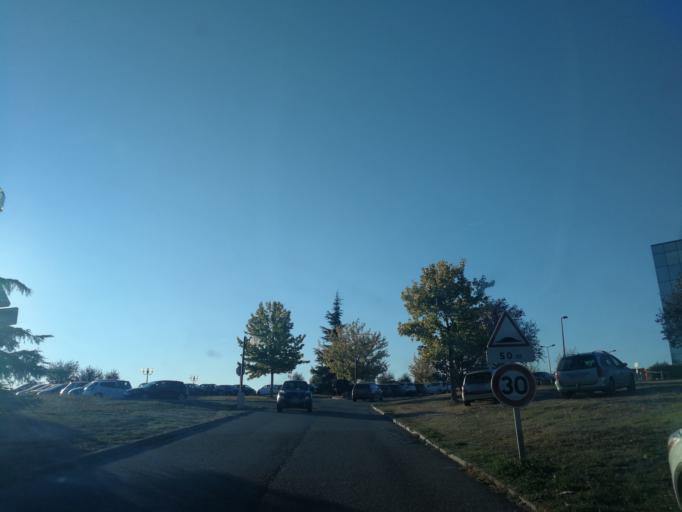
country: FR
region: Midi-Pyrenees
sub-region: Departement de la Haute-Garonne
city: Montrabe
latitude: 43.6501
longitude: 1.5106
